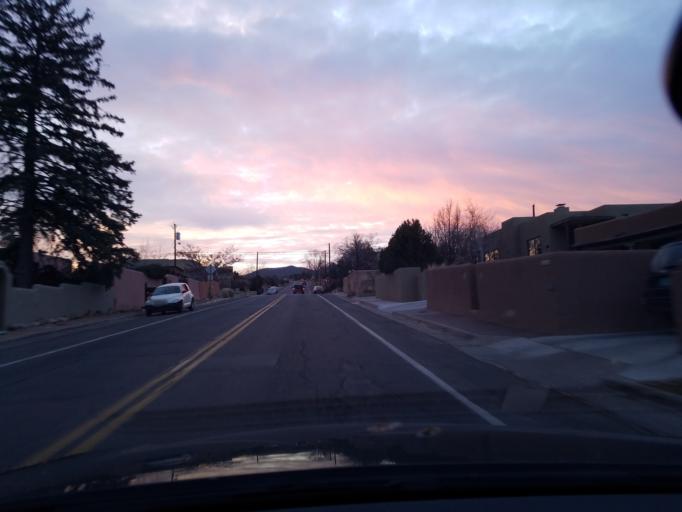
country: US
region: New Mexico
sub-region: Santa Fe County
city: Santa Fe
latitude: 35.6928
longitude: -105.9335
